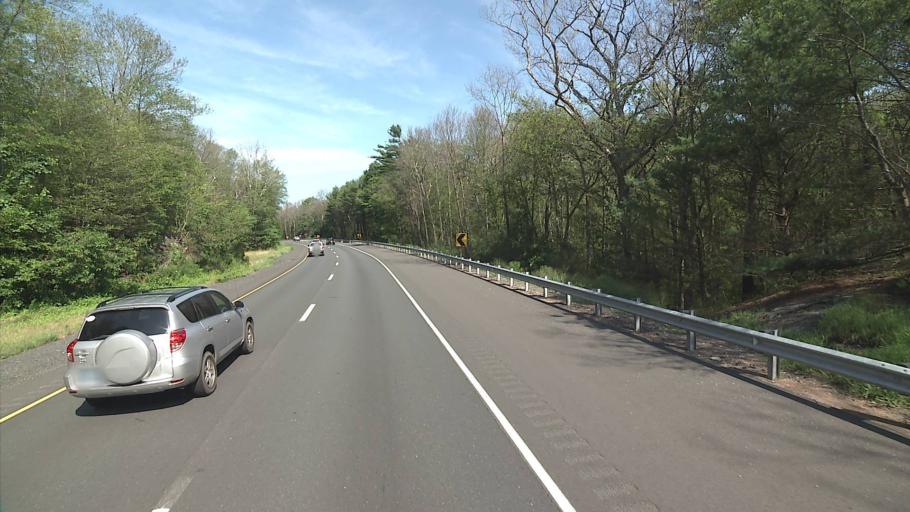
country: US
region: Connecticut
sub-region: Hartford County
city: Terramuggus
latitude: 41.6574
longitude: -72.5045
